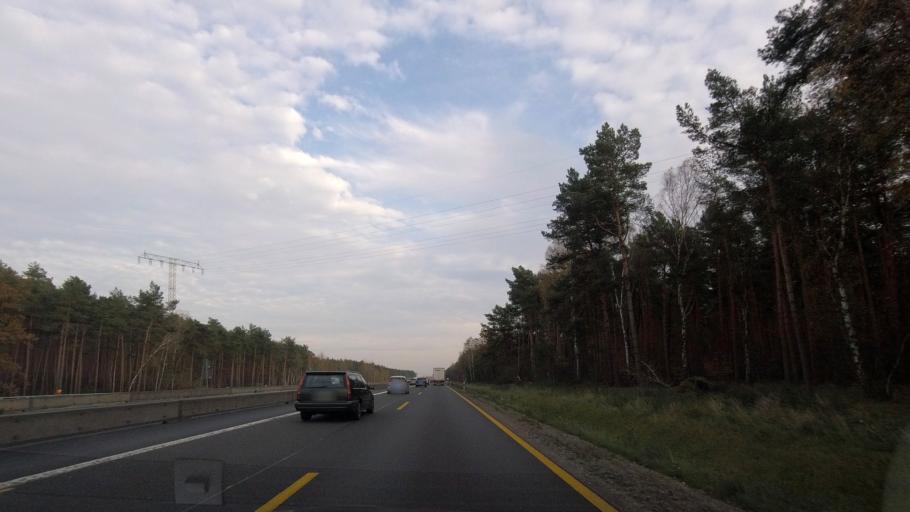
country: DE
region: Brandenburg
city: Michendorf
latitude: 52.3032
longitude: 12.9816
